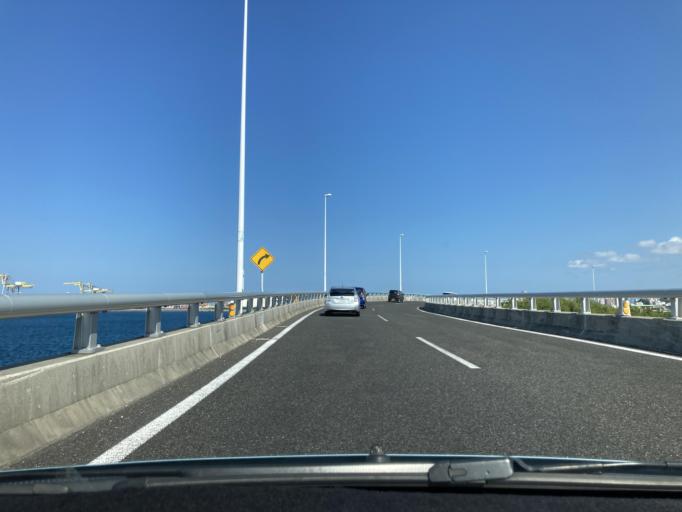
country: JP
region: Okinawa
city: Naha-shi
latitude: 26.2229
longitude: 127.6717
